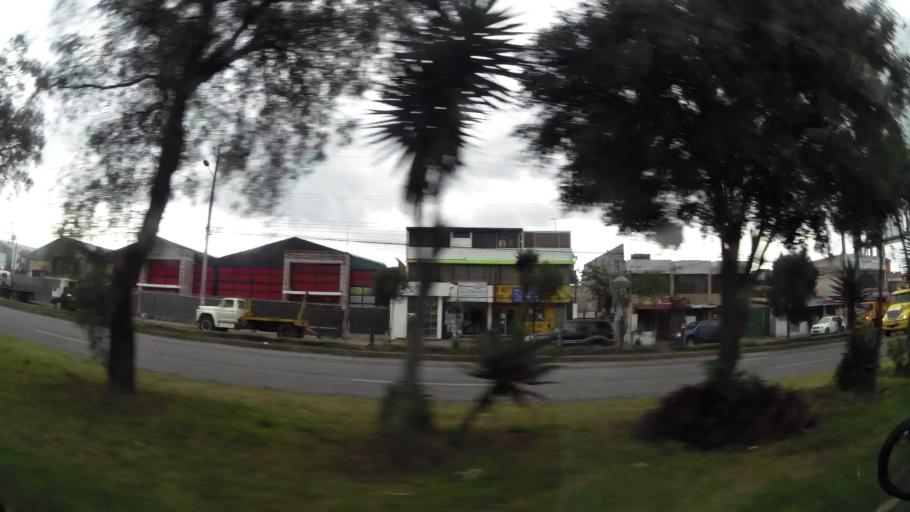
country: EC
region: Pichincha
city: Quito
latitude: -0.1080
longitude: -78.4499
